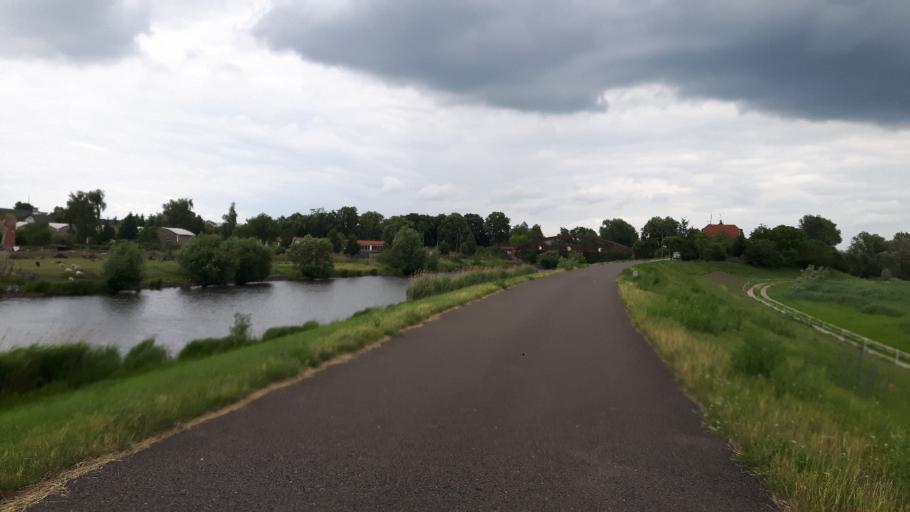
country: DE
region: Brandenburg
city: Schwedt (Oder)
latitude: 53.0454
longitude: 14.2715
